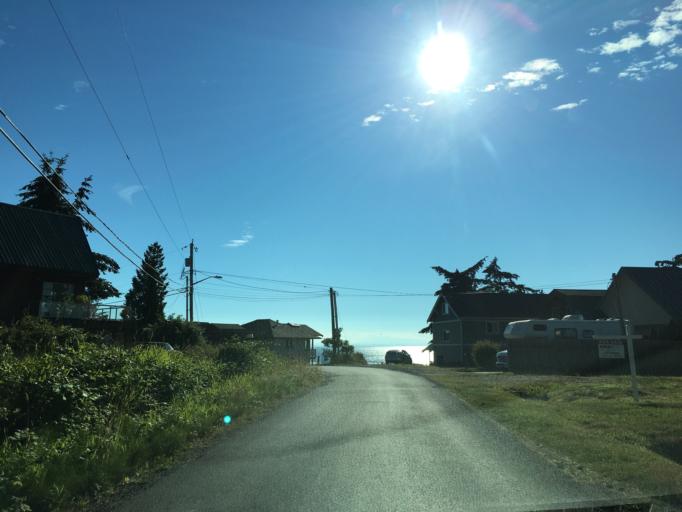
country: US
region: Washington
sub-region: Whatcom County
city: Birch Bay
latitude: 48.9142
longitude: -122.7449
